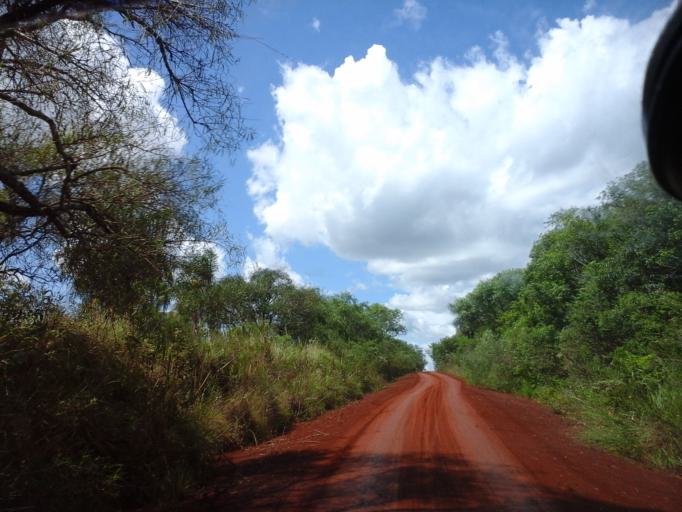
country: AR
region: Misiones
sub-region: Departamento de Apostoles
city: Apostoles
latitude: -27.9785
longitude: -55.7762
